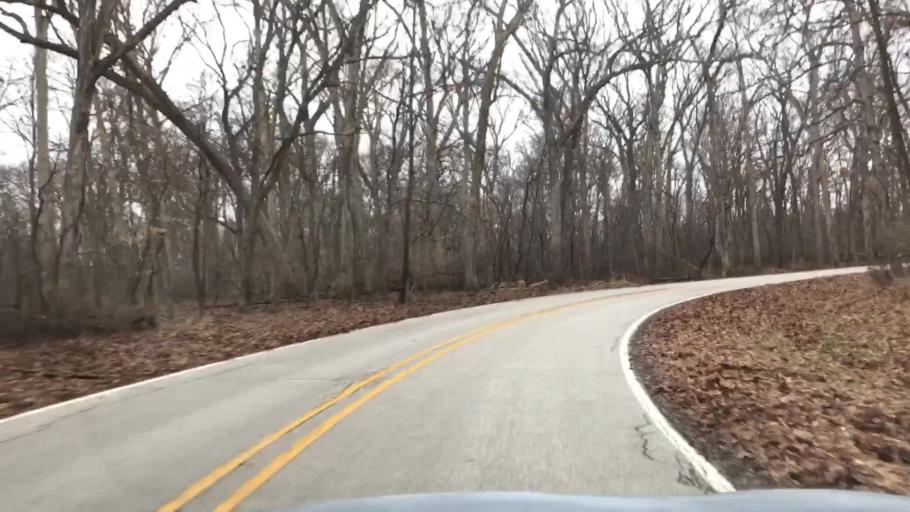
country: US
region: Illinois
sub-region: McLean County
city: Hudson
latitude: 40.6422
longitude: -88.9142
